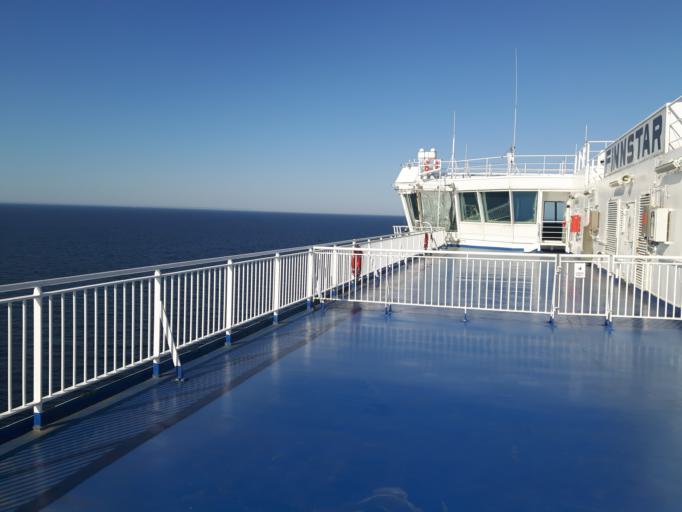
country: SE
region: Gotland
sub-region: Gotland
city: Hemse
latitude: 56.5973
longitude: 17.9596
